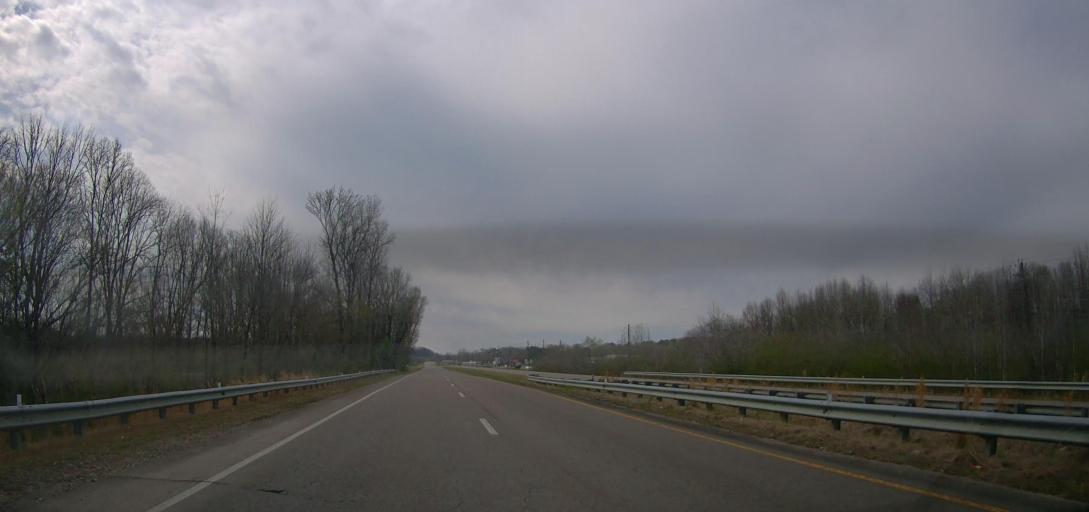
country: US
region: Alabama
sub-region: Walker County
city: Carbon Hill
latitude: 33.8822
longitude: -87.5114
